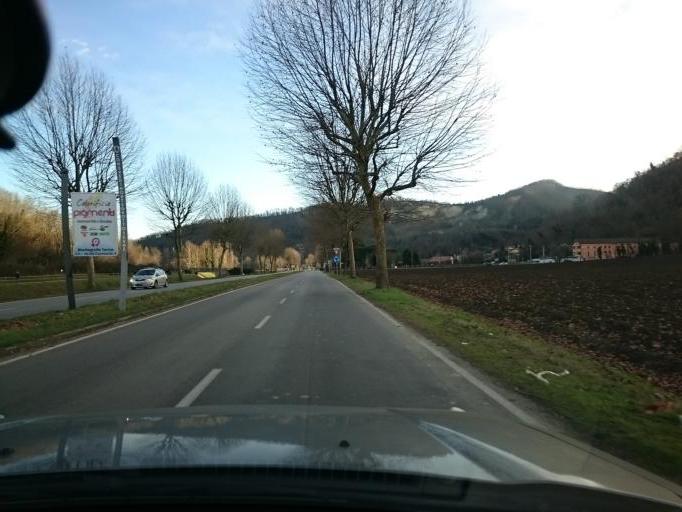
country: IT
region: Veneto
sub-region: Provincia di Padova
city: Montegrotto Terme
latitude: 45.3292
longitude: 11.7746
